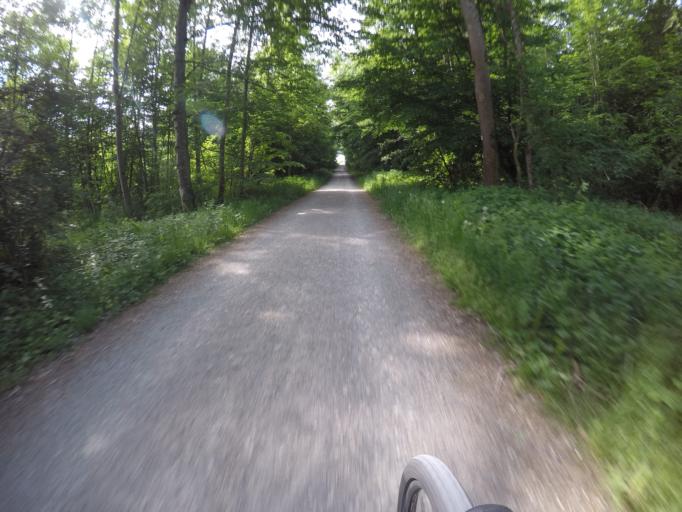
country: DE
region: Baden-Wuerttemberg
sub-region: Regierungsbezirk Stuttgart
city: Denkendorf
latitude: 48.6677
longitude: 9.3199
